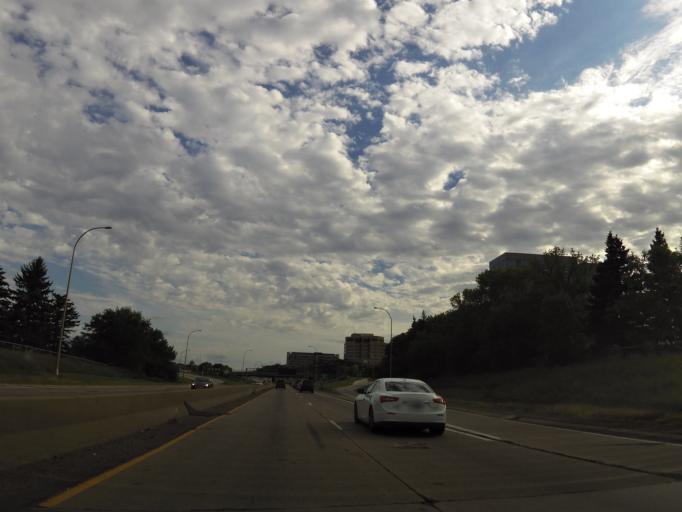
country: US
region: Minnesota
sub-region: Hennepin County
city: Edina
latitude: 44.9028
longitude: -93.4015
